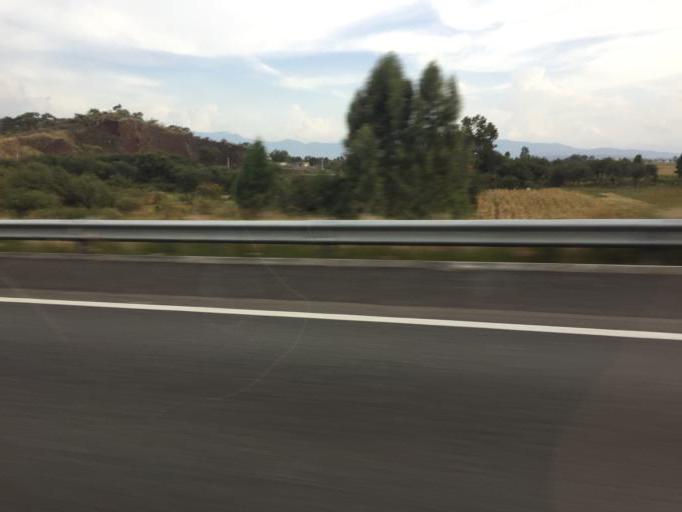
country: MX
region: Michoacan
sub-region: Alvaro Obregon
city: Tzintzimeo
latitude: 19.8911
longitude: -100.9867
